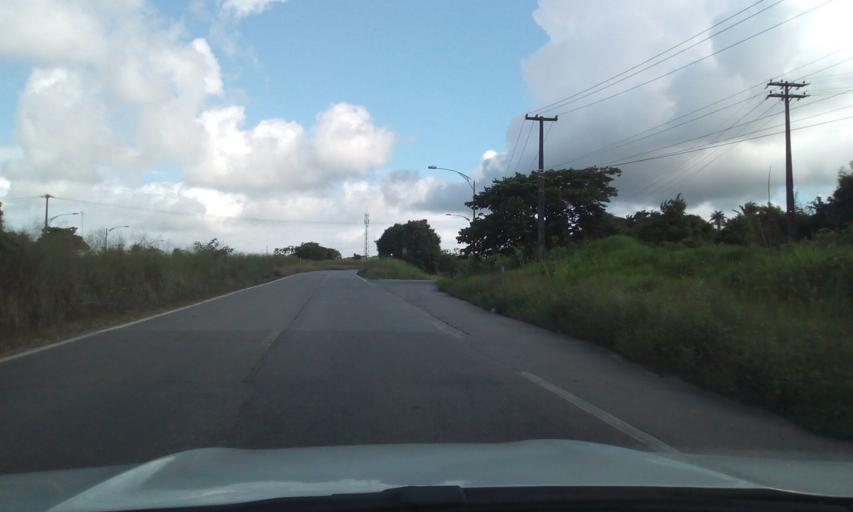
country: BR
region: Pernambuco
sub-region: Paulista
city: Paulista
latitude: -7.9440
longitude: -34.9044
